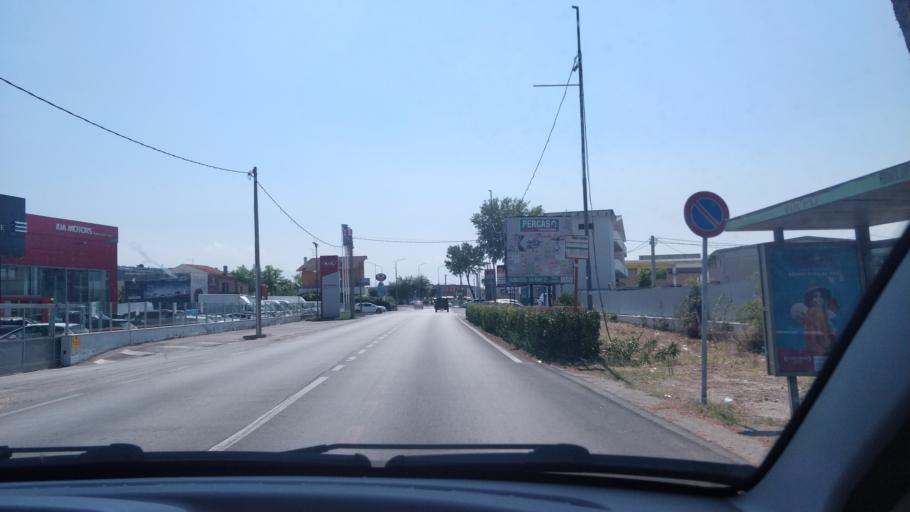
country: IT
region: Abruzzo
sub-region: Provincia di Chieti
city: Sambuceto
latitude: 42.4177
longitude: 14.1727
